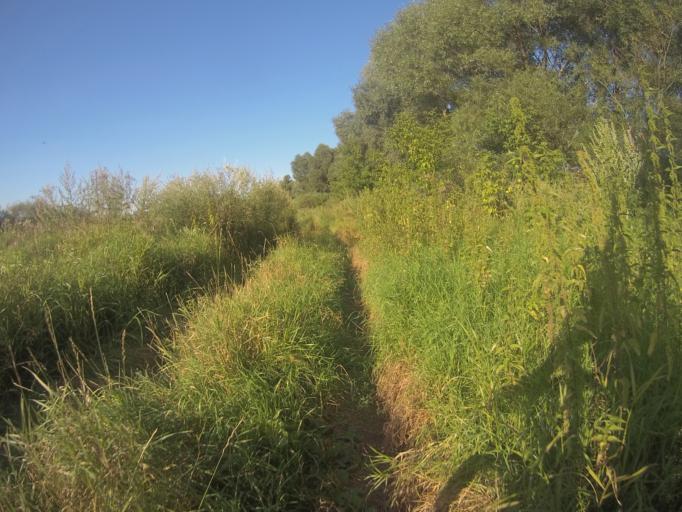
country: RU
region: Vladimir
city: Bogolyubovo
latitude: 56.1499
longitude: 40.4872
